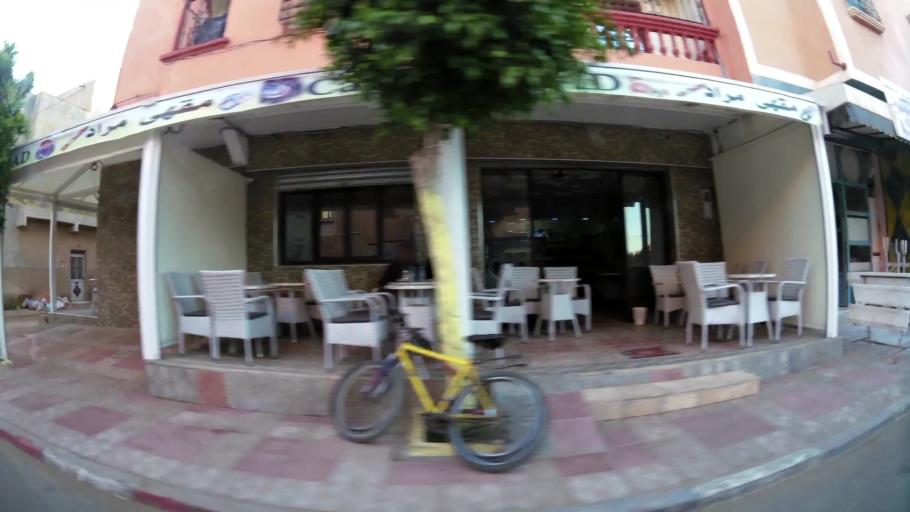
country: MA
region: Marrakech-Tensift-Al Haouz
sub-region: Kelaa-Des-Sraghna
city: Sidi Abdallah
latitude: 32.2381
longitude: -7.9527
